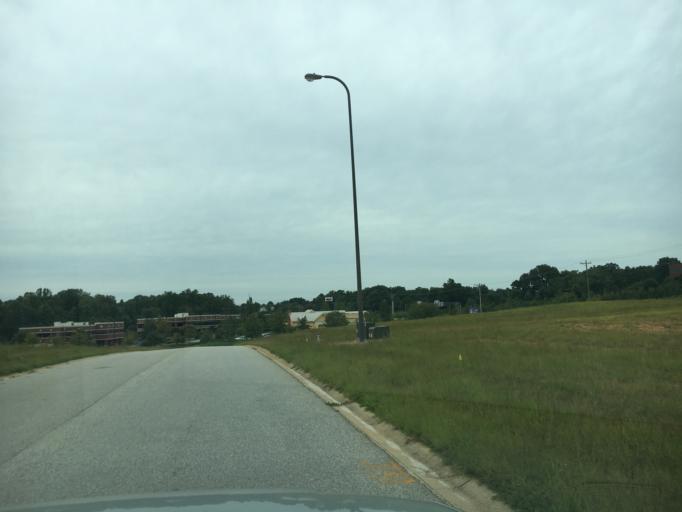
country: US
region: South Carolina
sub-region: Greenville County
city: Mauldin
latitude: 34.8065
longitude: -82.2851
